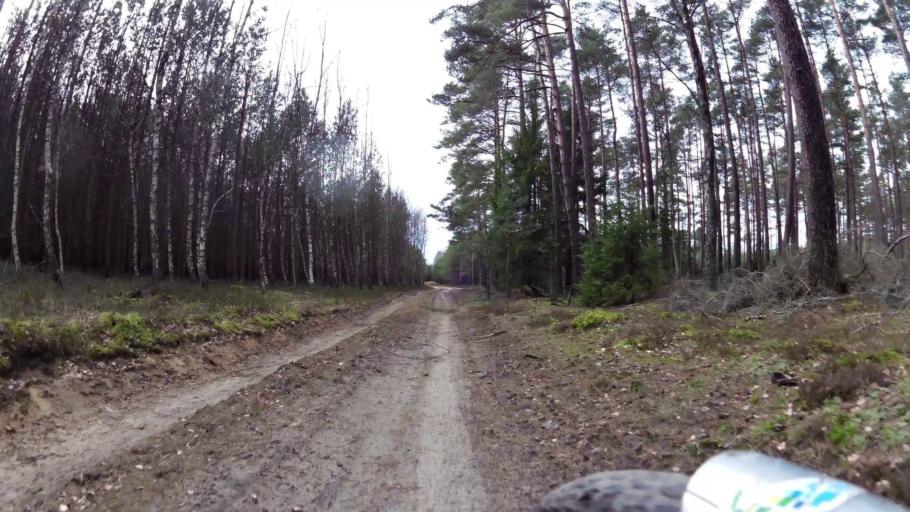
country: PL
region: Pomeranian Voivodeship
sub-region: Powiat bytowski
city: Trzebielino
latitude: 54.1510
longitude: 17.1713
